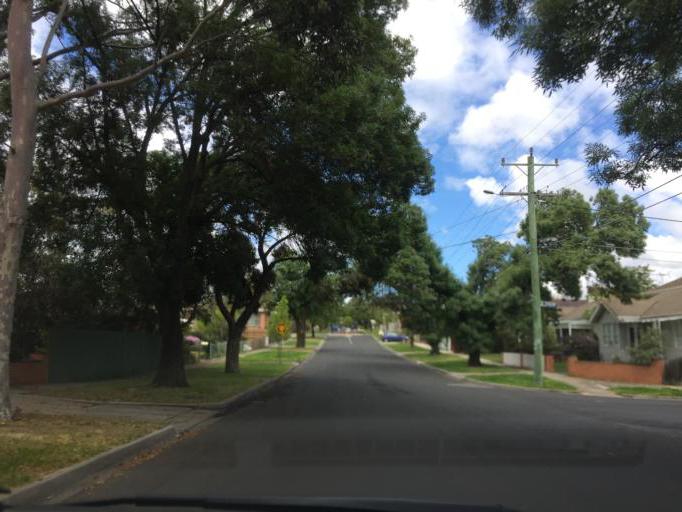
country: AU
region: Victoria
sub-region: Maribyrnong
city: Braybrook
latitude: -37.7903
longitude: 144.8406
